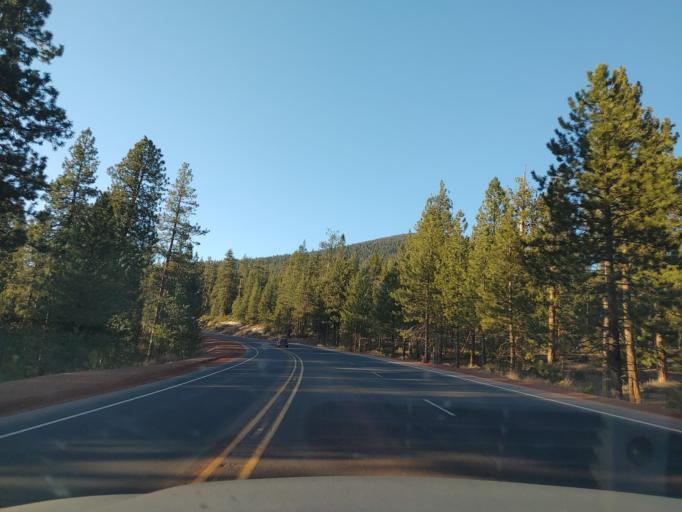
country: US
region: Oregon
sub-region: Deschutes County
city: La Pine
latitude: 43.4485
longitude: -121.8692
